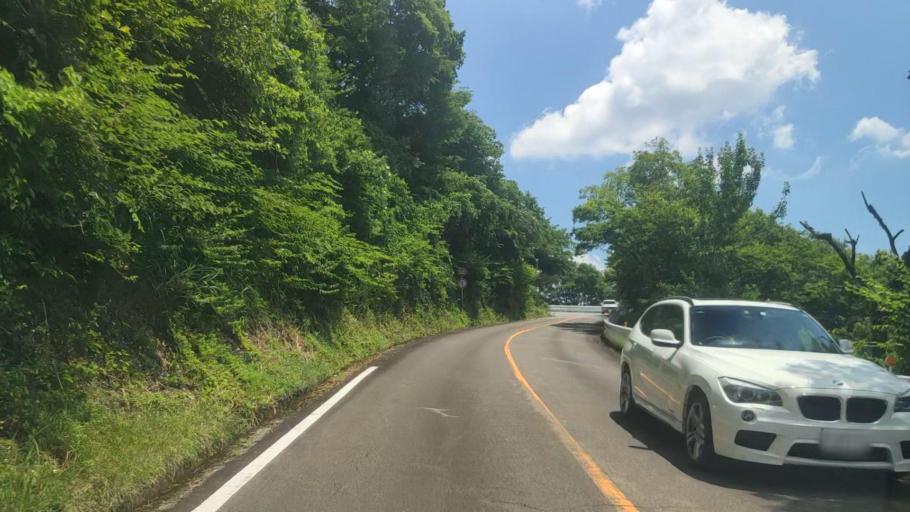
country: JP
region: Gifu
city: Tarui
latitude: 35.3810
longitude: 136.4524
